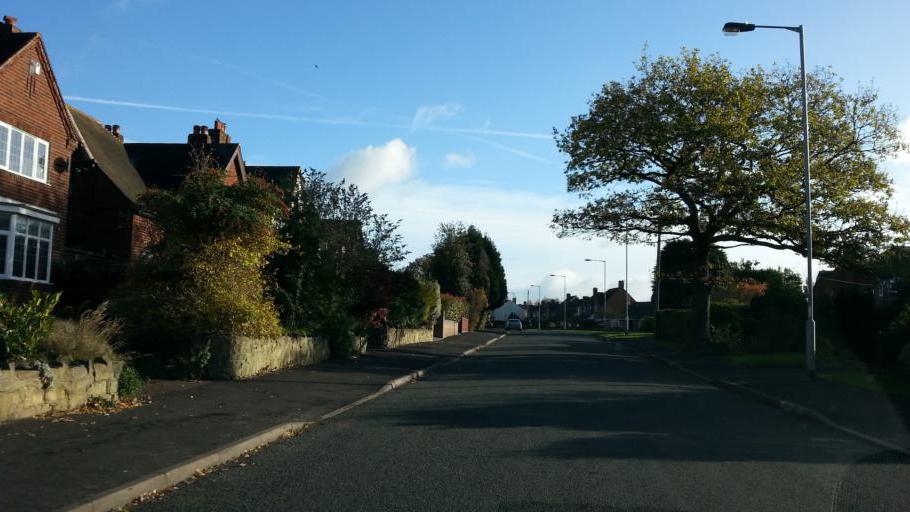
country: GB
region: England
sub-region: Staffordshire
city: Cannock
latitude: 52.6893
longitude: -2.0457
